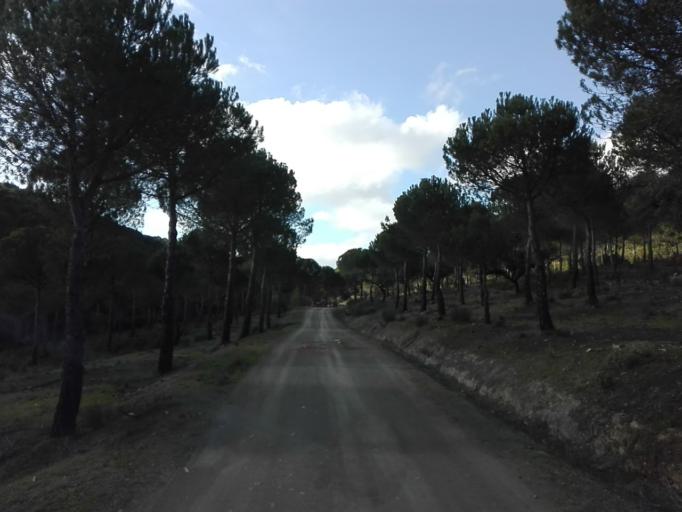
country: ES
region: Extremadura
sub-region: Provincia de Badajoz
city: Casas de Reina
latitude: 38.1777
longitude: -5.9732
